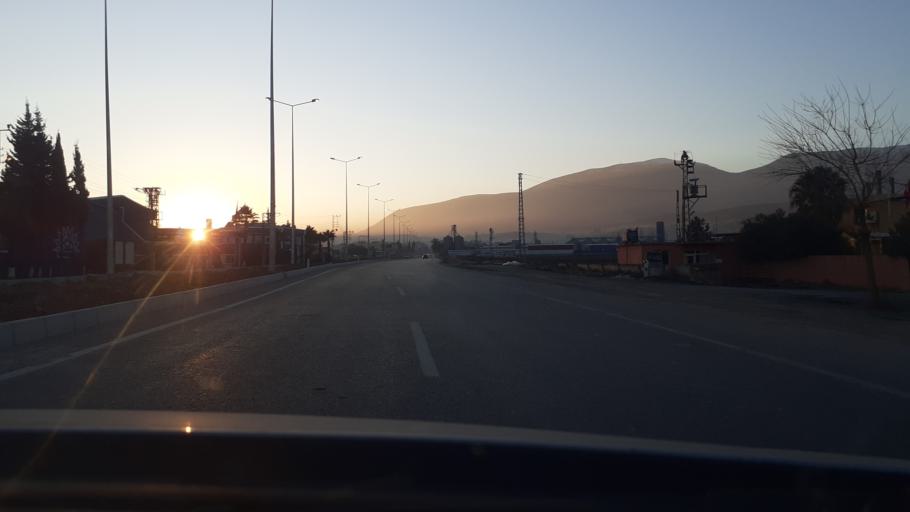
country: TR
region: Hatay
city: Kirikhan
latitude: 36.5019
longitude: 36.3887
